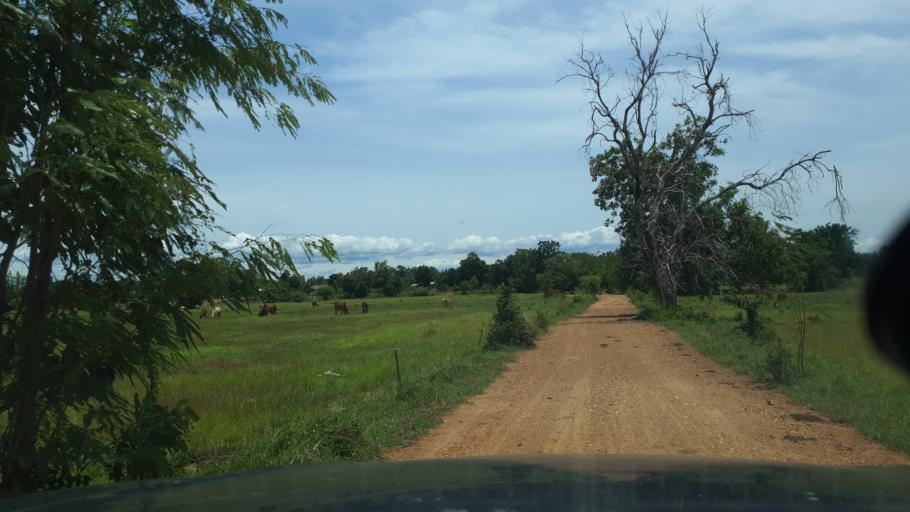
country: TH
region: Sukhothai
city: Ban Na
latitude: 17.0821
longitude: 99.6903
